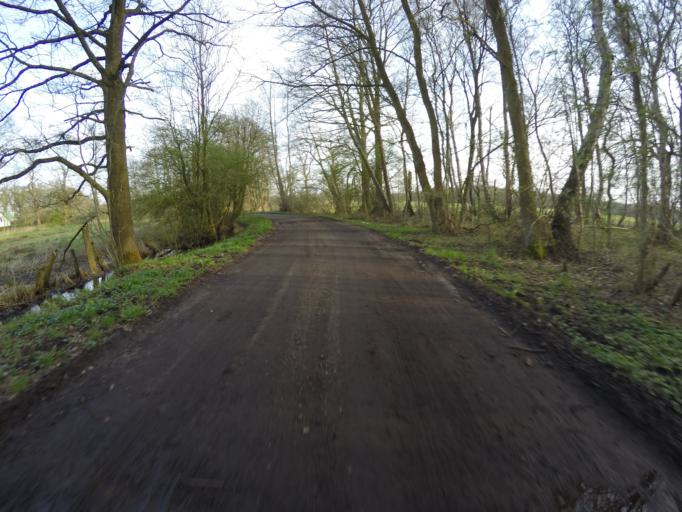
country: DE
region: Schleswig-Holstein
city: Hemdingen
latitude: 53.7313
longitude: 9.8281
